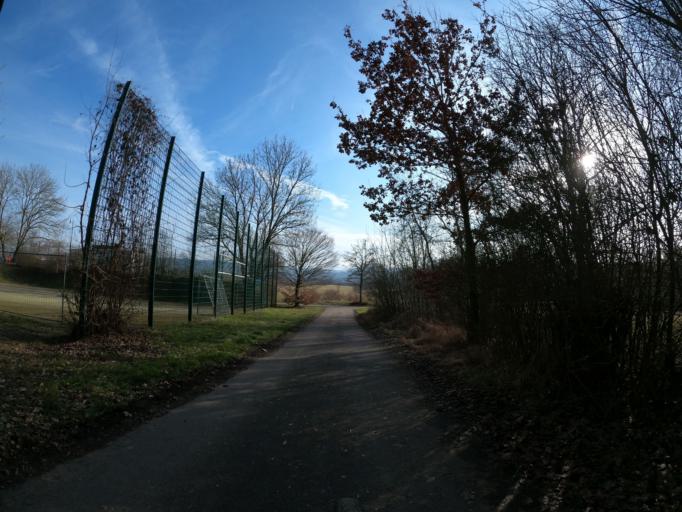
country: DE
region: Baden-Wuerttemberg
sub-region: Tuebingen Region
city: Metzingen
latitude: 48.5335
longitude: 9.2663
